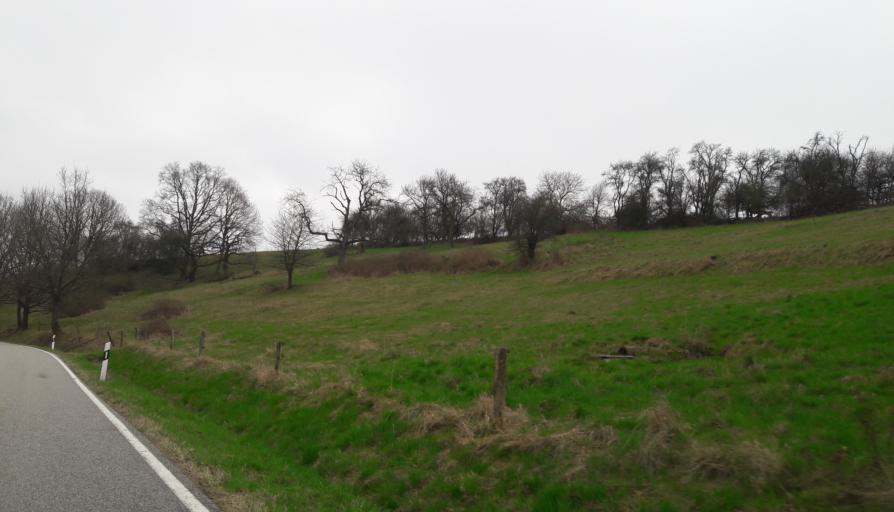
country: DE
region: Rheinland-Pfalz
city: Borsborn
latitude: 49.4365
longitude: 7.4085
